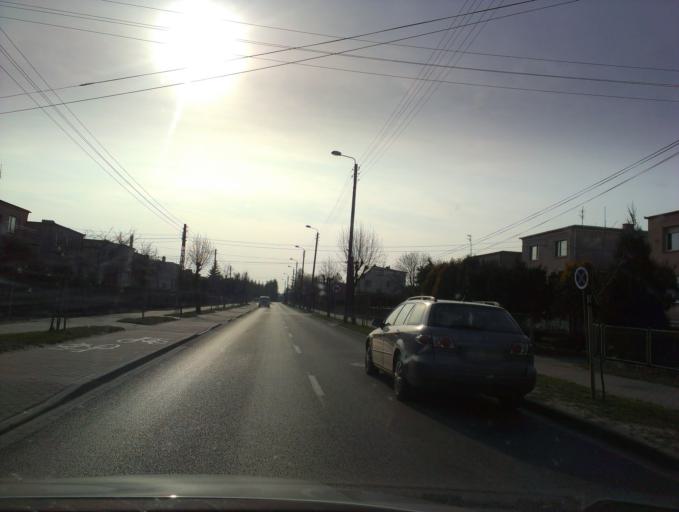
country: PL
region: Kujawsko-Pomorskie
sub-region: Powiat sepolenski
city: Sepolno Krajenskie
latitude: 53.4497
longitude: 17.5191
